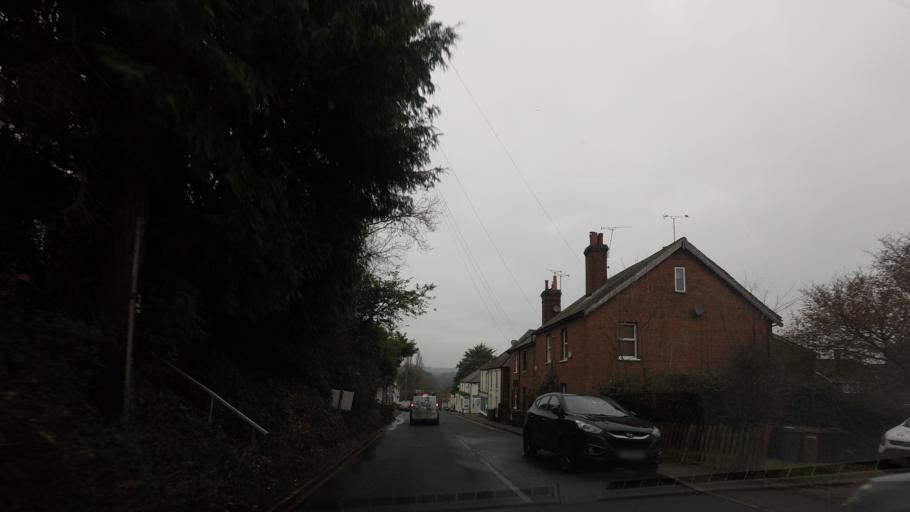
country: GB
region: England
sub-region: Kent
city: Hawkhurst
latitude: 51.0496
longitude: 0.5098
